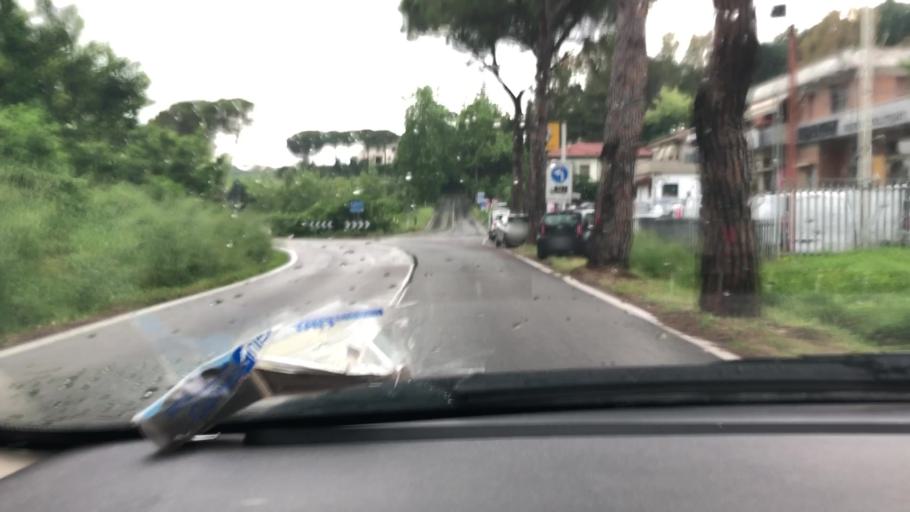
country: IT
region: Tuscany
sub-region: Province of Pisa
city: Pontedera
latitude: 43.6793
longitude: 10.6374
